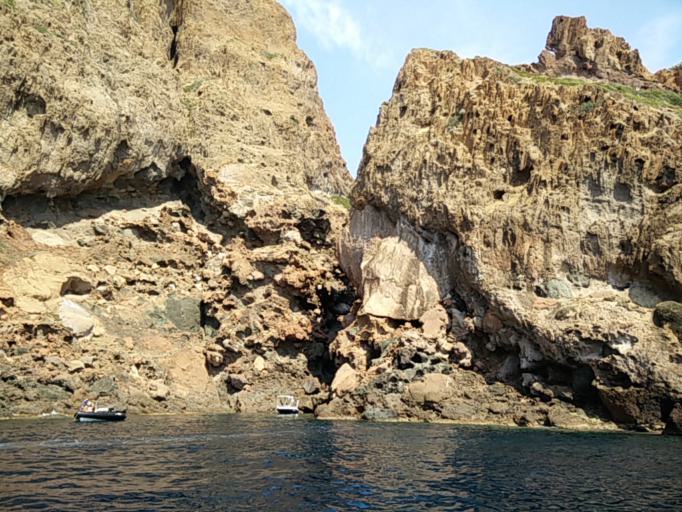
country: FR
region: Corsica
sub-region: Departement de la Corse-du-Sud
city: Cargese
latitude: 42.3460
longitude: 8.5538
